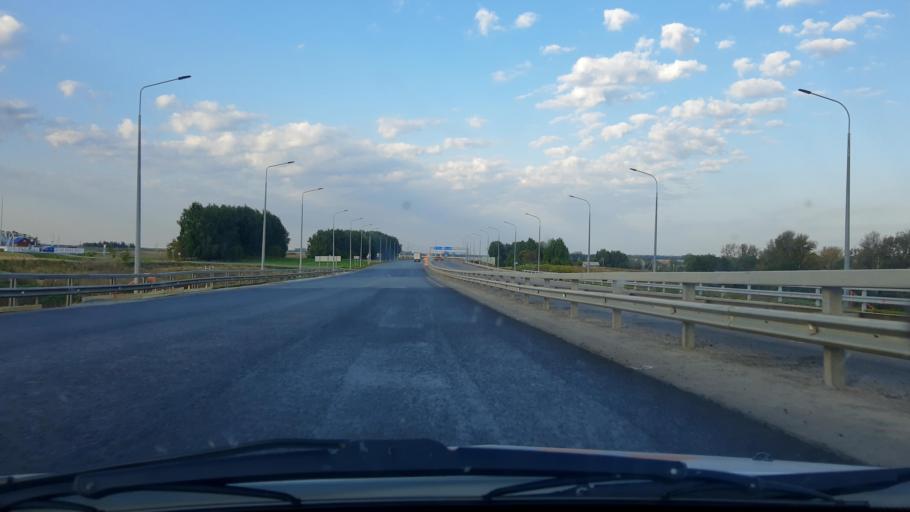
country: RU
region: Bashkortostan
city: Buzdyak
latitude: 54.6312
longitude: 54.4668
